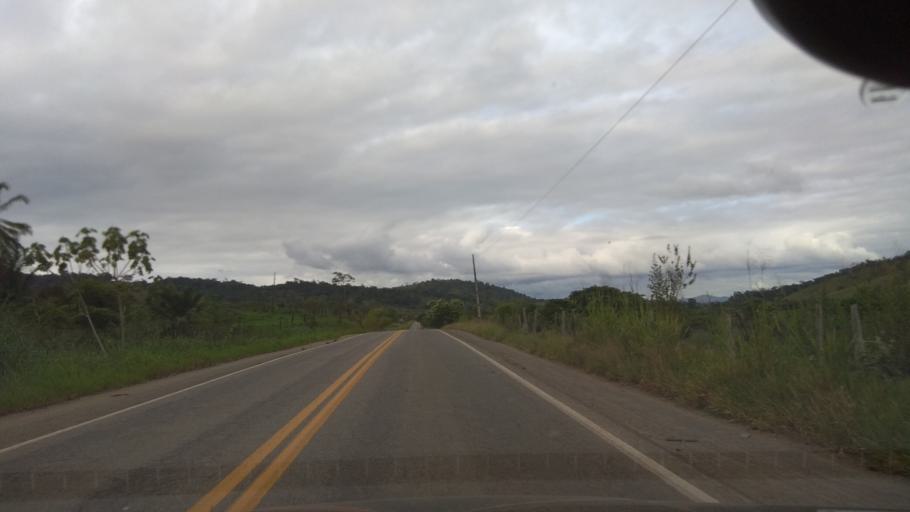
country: BR
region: Bahia
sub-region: Ipiau
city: Ipiau
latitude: -14.1446
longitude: -39.7144
